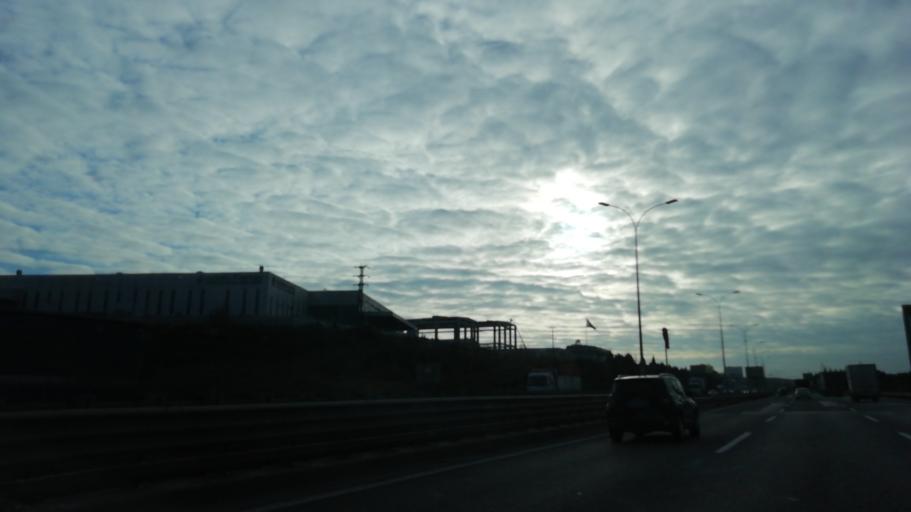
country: TR
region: Kocaeli
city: Balcik
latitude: 40.8646
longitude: 29.4000
